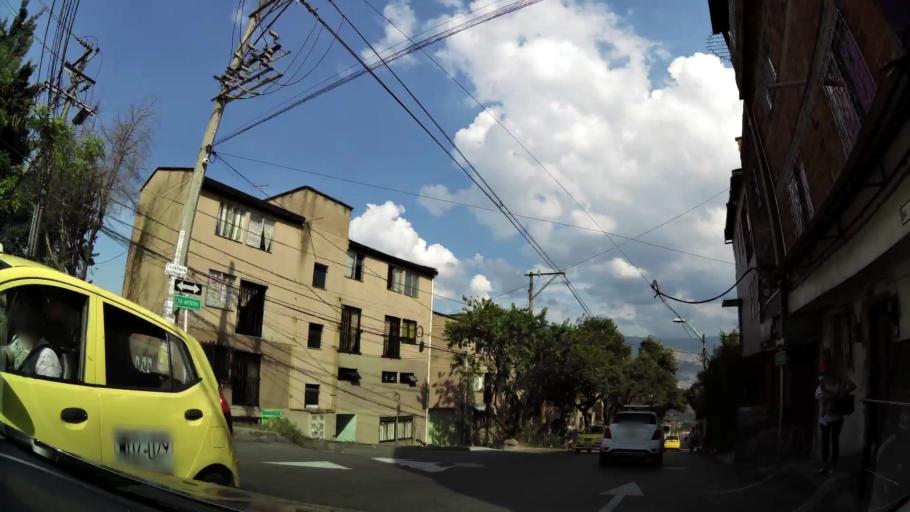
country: CO
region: Antioquia
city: Medellin
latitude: 6.2877
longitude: -75.5884
